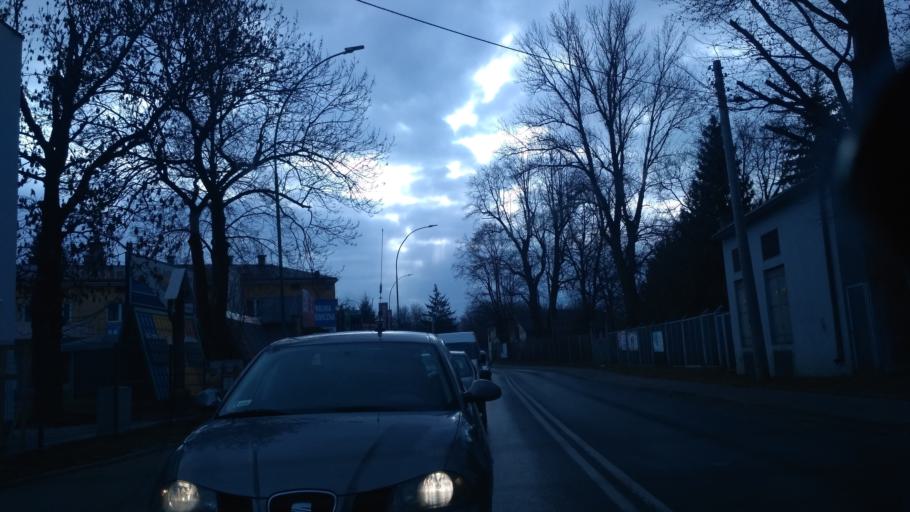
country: PL
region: Subcarpathian Voivodeship
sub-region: Powiat lancucki
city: Lancut
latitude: 50.0805
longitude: 22.2330
